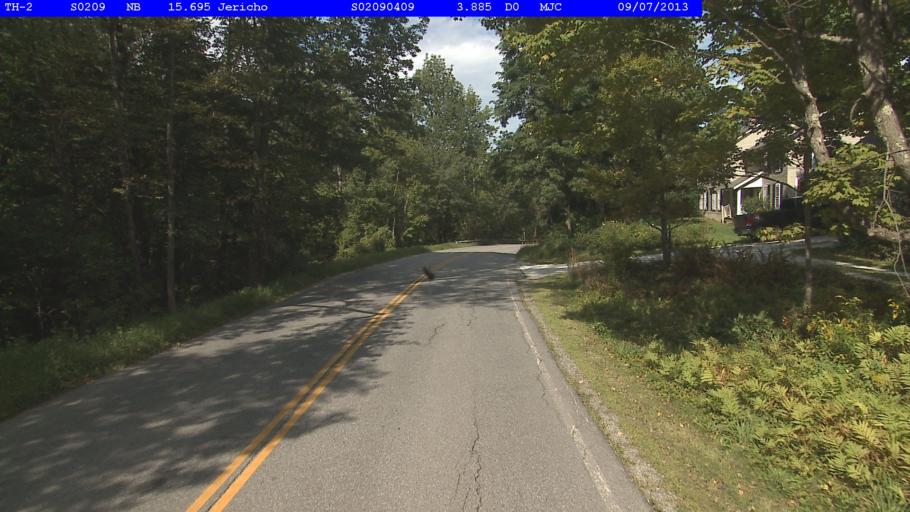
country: US
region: Vermont
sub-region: Chittenden County
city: Jericho
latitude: 44.4814
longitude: -72.9716
